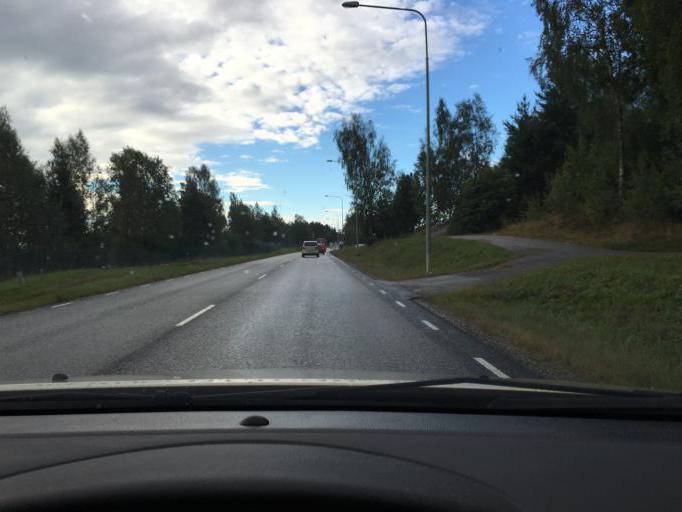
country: SE
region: Stockholm
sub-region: Sodertalje Kommun
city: Pershagen
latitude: 59.1691
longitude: 17.6382
